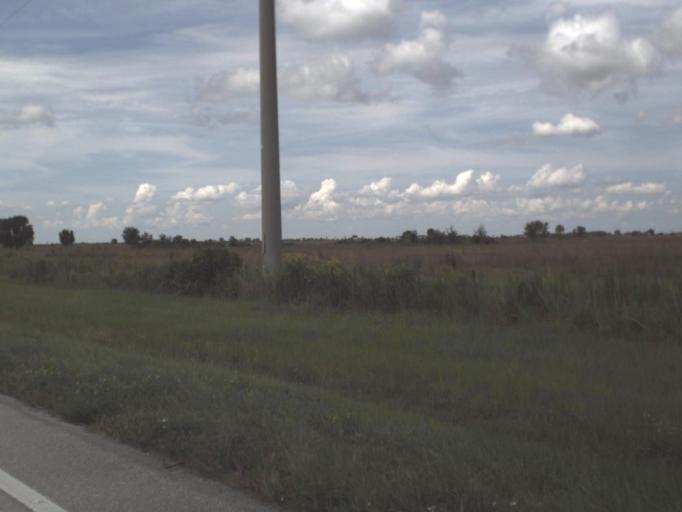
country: US
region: Florida
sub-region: Highlands County
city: Placid Lakes
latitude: 27.2090
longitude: -81.5088
